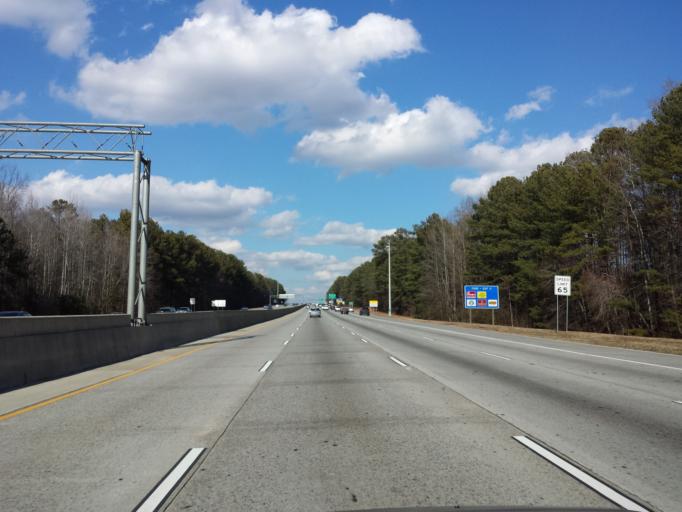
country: US
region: Georgia
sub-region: Fulton County
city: Alpharetta
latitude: 34.0756
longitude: -84.2683
